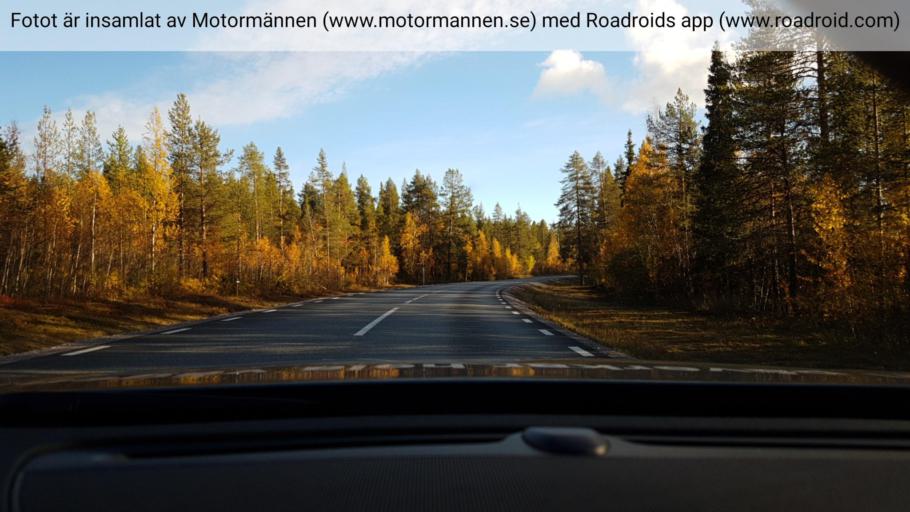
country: SE
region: Norrbotten
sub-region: Jokkmokks Kommun
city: Jokkmokk
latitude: 66.9181
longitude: 19.8312
